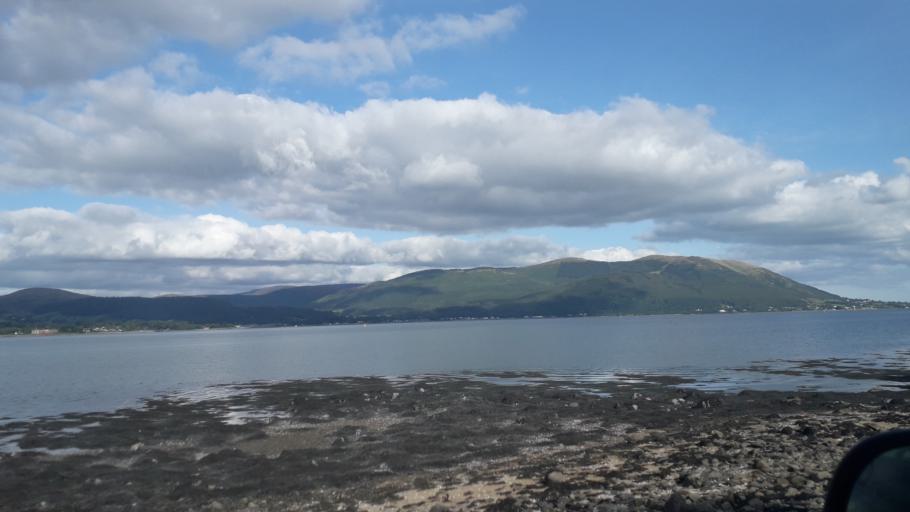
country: GB
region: Northern Ireland
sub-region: Down District
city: Warrenpoint
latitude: 54.0878
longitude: -6.2540
